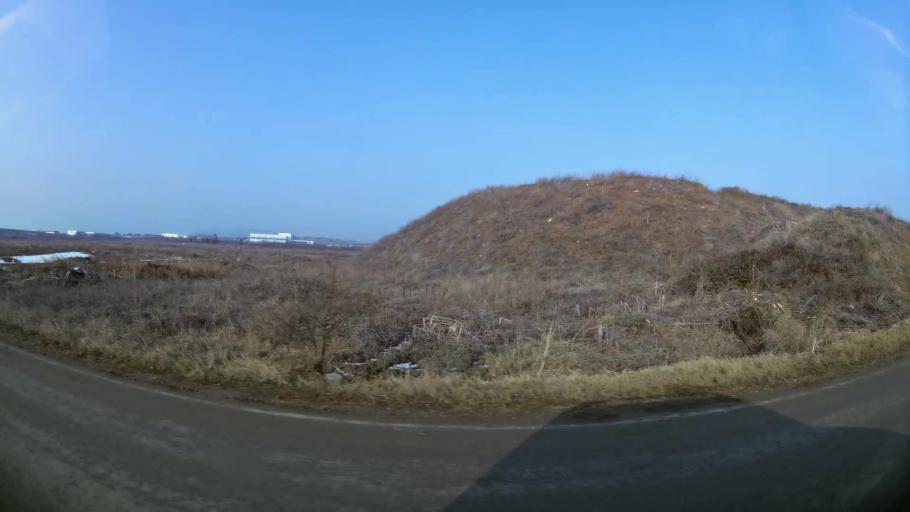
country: MK
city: Miladinovci
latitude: 41.9776
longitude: 21.6249
